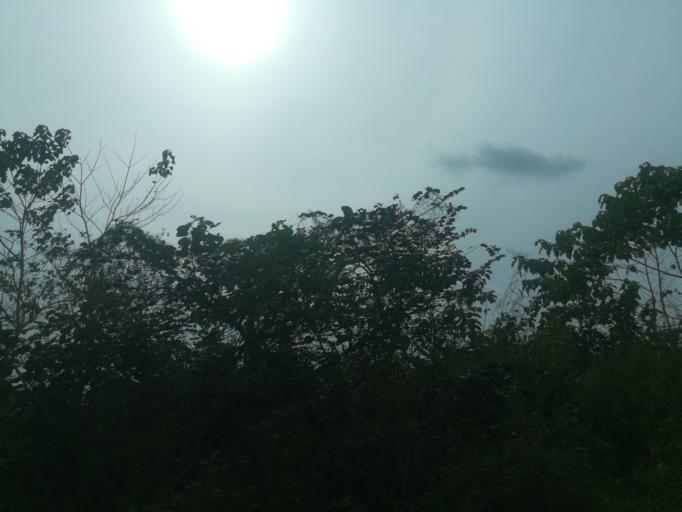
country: NG
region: Ogun
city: Ayetoro
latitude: 7.3080
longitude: 3.0731
